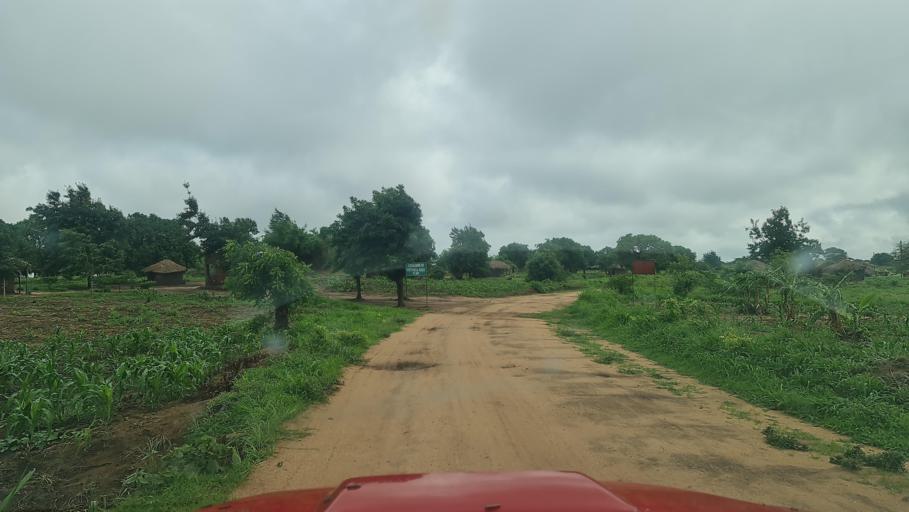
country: MW
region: Southern Region
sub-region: Nsanje District
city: Nsanje
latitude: -17.1933
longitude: 35.7019
